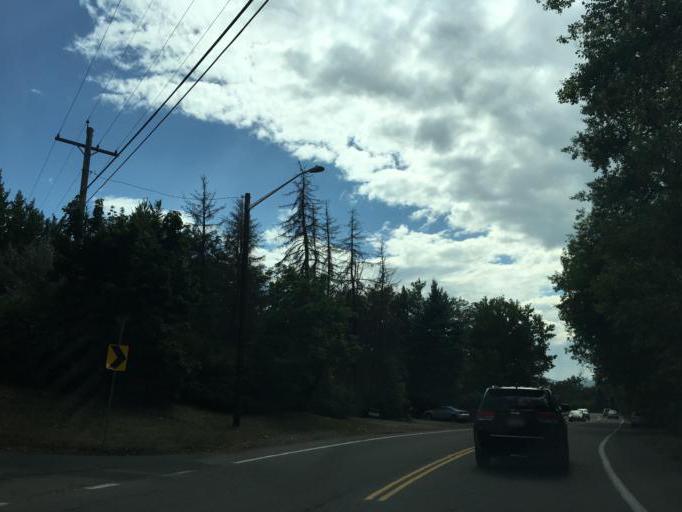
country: US
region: Colorado
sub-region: Jefferson County
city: Applewood
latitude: 39.7415
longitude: -105.1425
